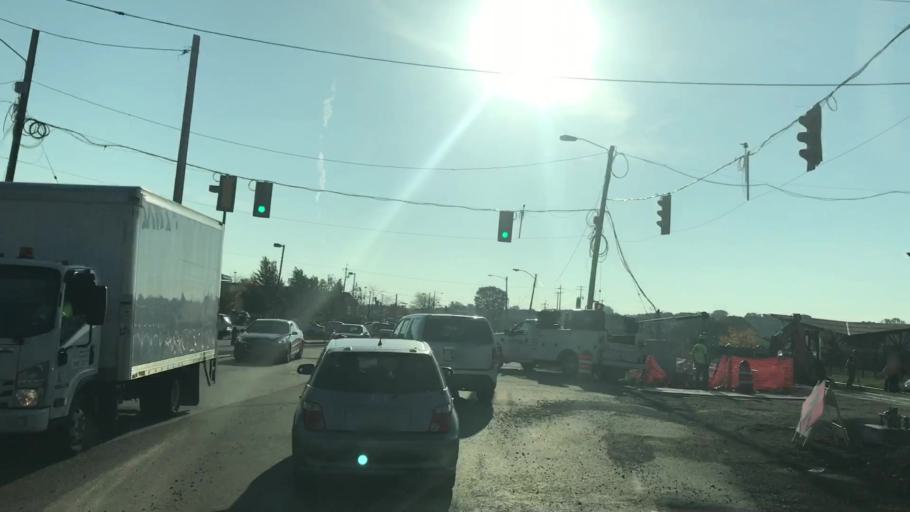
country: US
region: Wisconsin
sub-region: Milwaukee County
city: Wauwatosa
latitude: 43.0472
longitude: -88.0003
